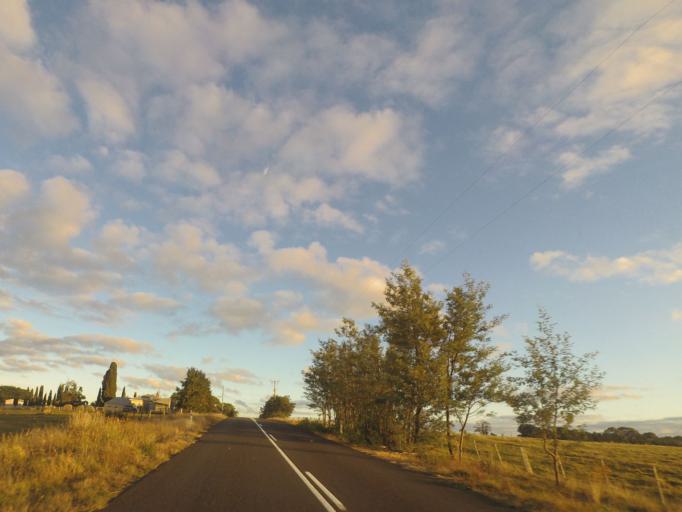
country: AU
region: Victoria
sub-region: Hume
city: Sunbury
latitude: -37.2829
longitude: 144.5119
